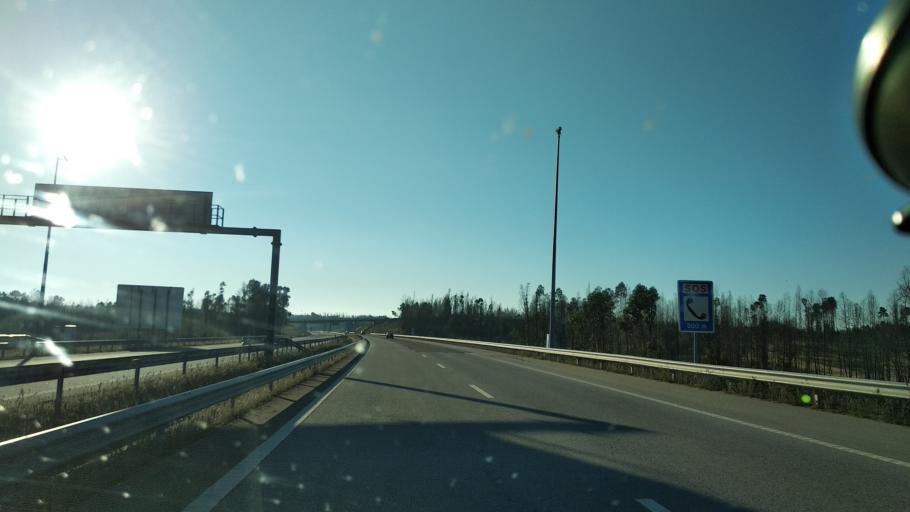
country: PT
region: Santarem
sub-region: Macao
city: Macao
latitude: 39.5346
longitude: -7.9351
